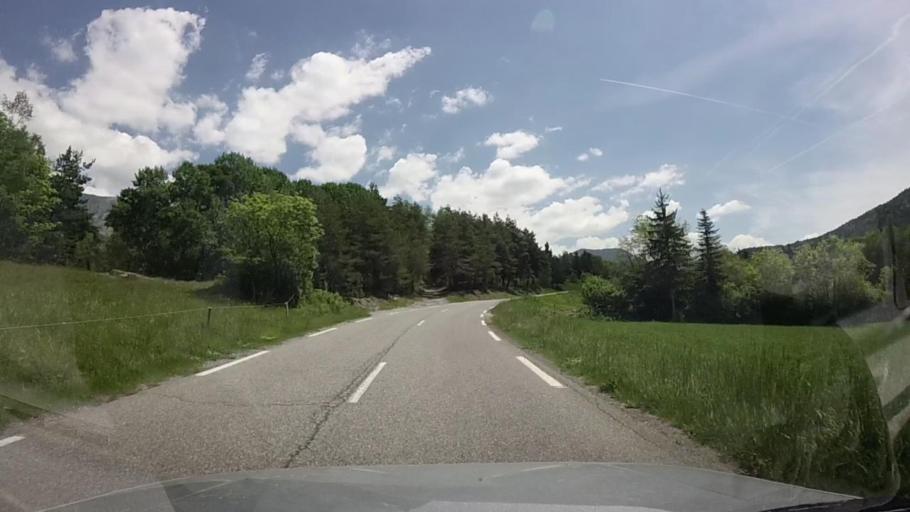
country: FR
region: Provence-Alpes-Cote d'Azur
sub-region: Departement des Alpes-de-Haute-Provence
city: Seyne-les-Alpes
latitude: 44.3372
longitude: 6.3848
